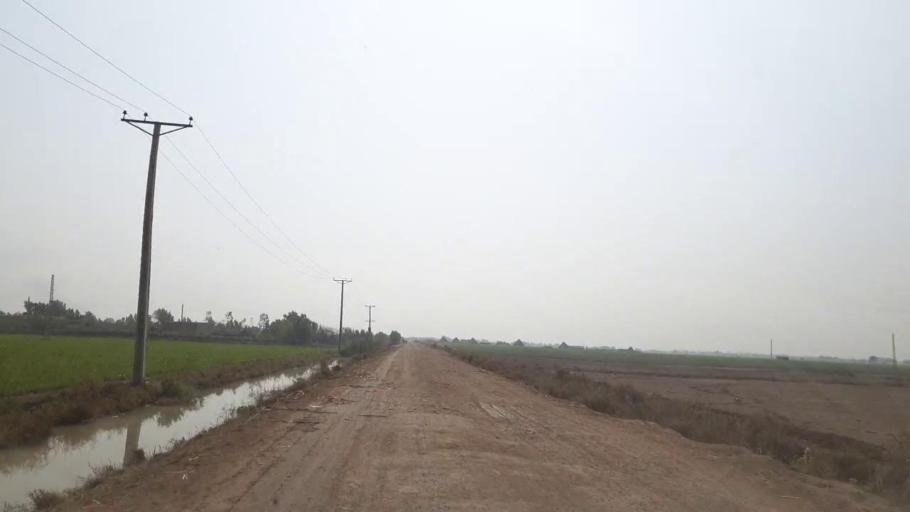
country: PK
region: Sindh
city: Mirpur Khas
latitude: 25.5451
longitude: 69.0599
